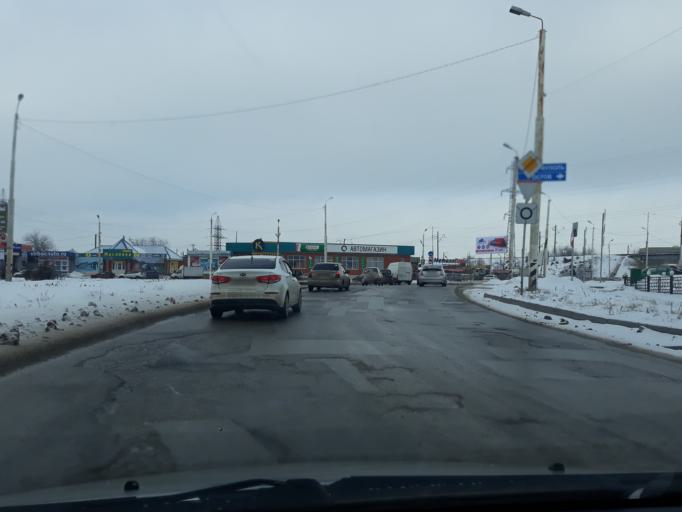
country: RU
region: Rostov
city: Taganrog
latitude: 47.2526
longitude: 38.8945
